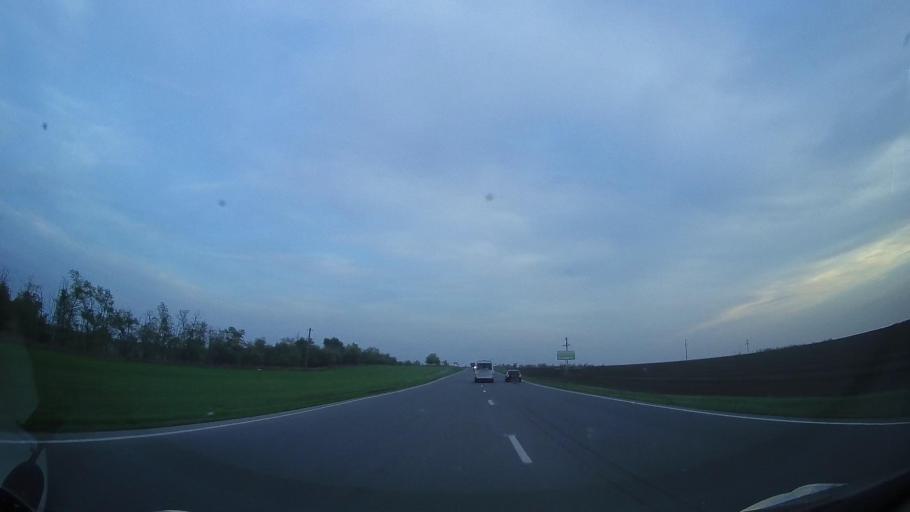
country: RU
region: Rostov
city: Kagal'nitskaya
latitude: 46.8960
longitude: 40.1271
